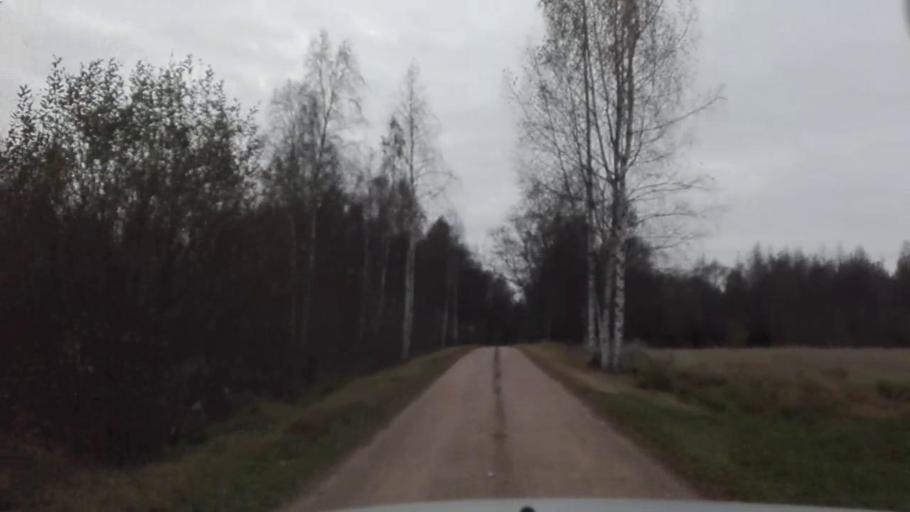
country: EE
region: Jogevamaa
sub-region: Poltsamaa linn
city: Poltsamaa
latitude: 58.3990
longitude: 25.9745
